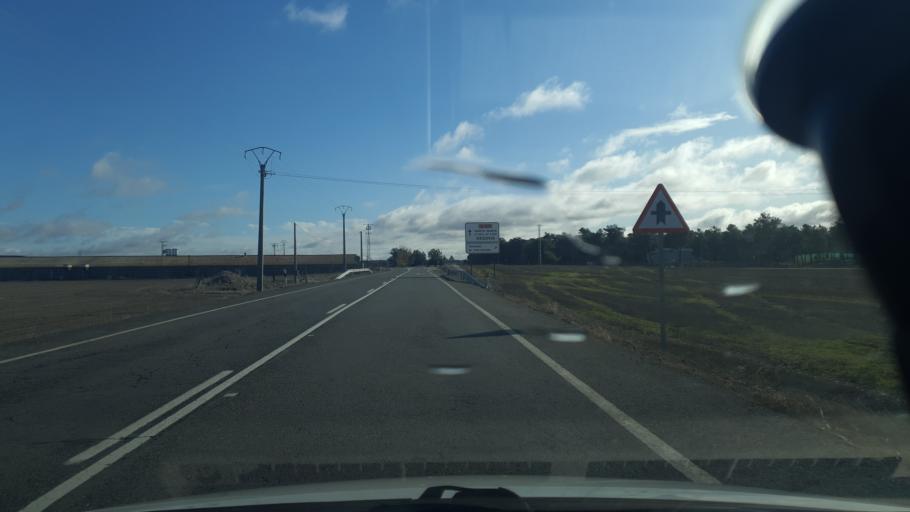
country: ES
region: Castille and Leon
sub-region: Provincia de Segovia
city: Martin Munoz de la Dehesa
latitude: 41.0467
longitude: -4.6861
